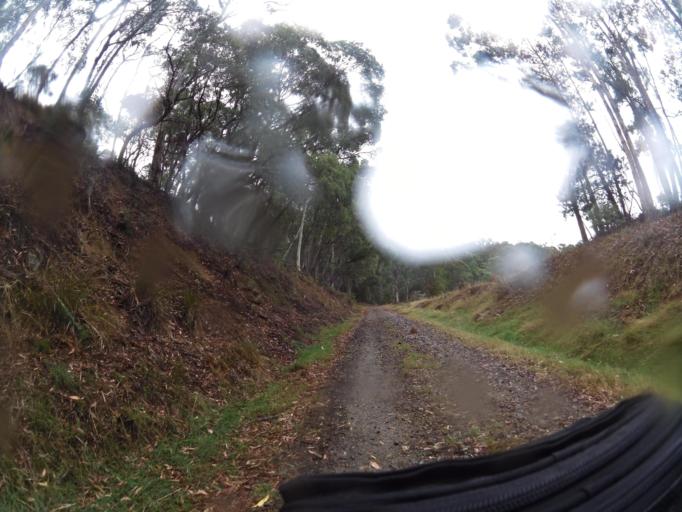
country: AU
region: New South Wales
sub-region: Greater Hume Shire
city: Holbrook
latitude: -36.2300
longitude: 147.5852
